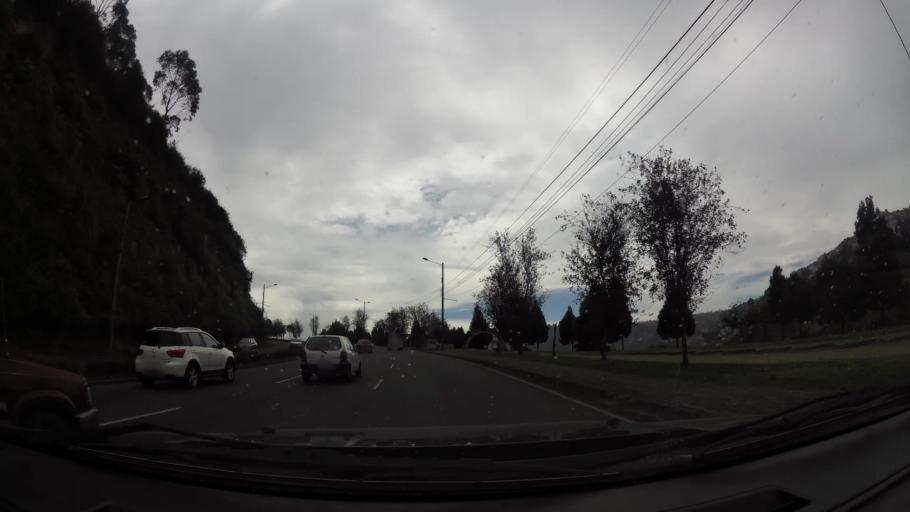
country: EC
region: Pichincha
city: Quito
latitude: -0.2264
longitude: -78.4983
